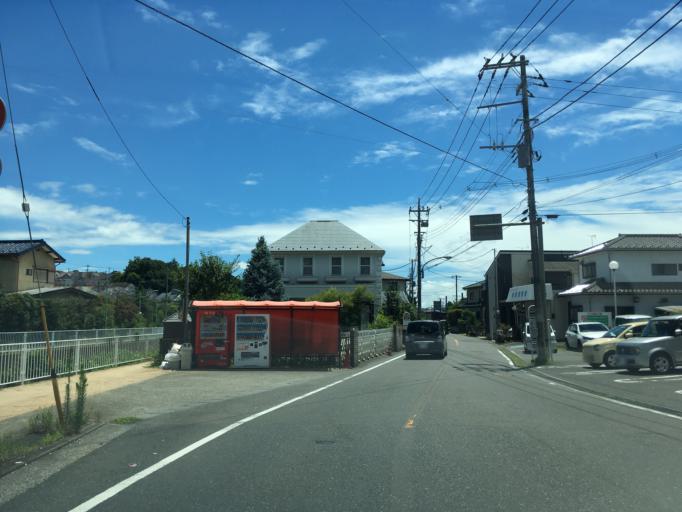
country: JP
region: Tokyo
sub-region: Machida-shi
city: Machida
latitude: 35.5540
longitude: 139.4898
